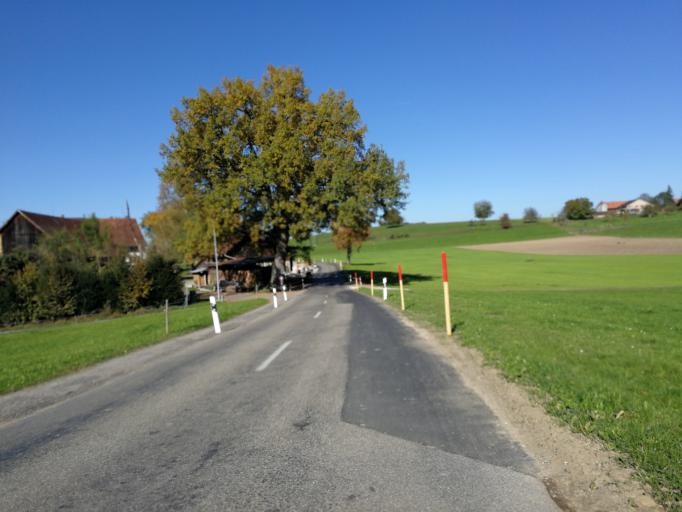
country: CH
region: Zurich
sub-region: Bezirk Hinwil
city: Wolfhausen
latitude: 47.2626
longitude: 8.7922
